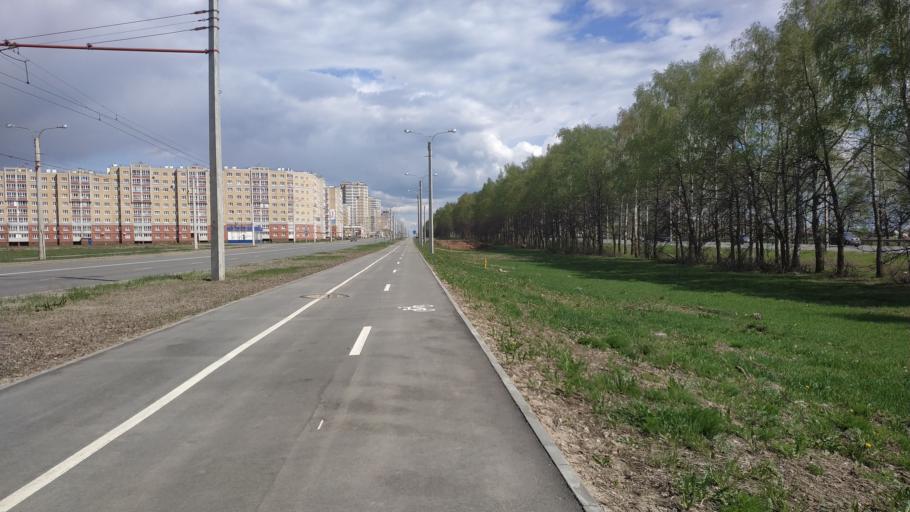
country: RU
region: Chuvashia
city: Novocheboksarsk
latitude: 56.1258
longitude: 47.3684
